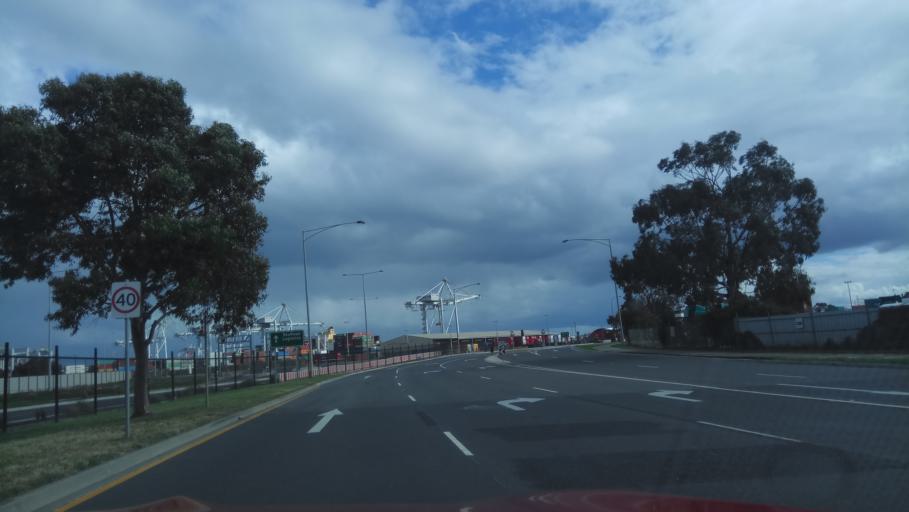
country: AU
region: Victoria
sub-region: Hobsons Bay
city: Williamstown
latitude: -37.8399
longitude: 144.9127
